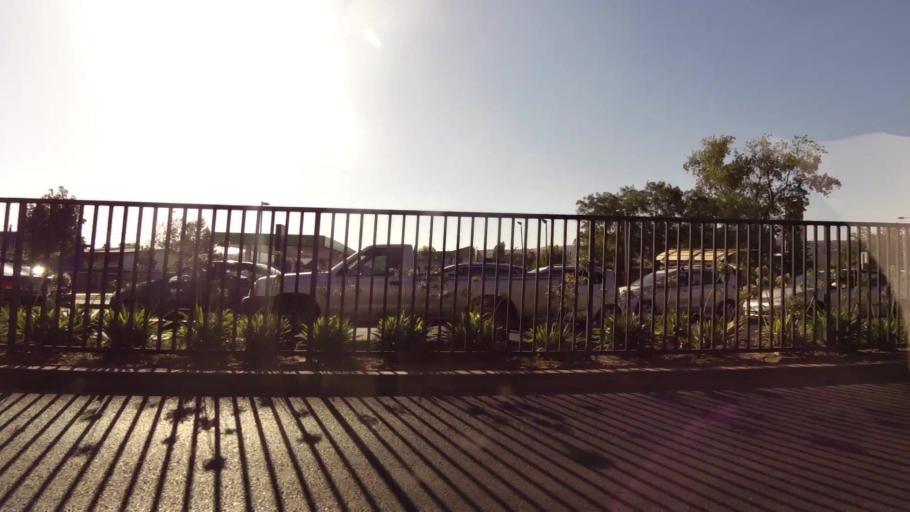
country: CL
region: Maule
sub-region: Provincia de Talca
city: Talca
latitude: -35.4381
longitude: -71.6818
